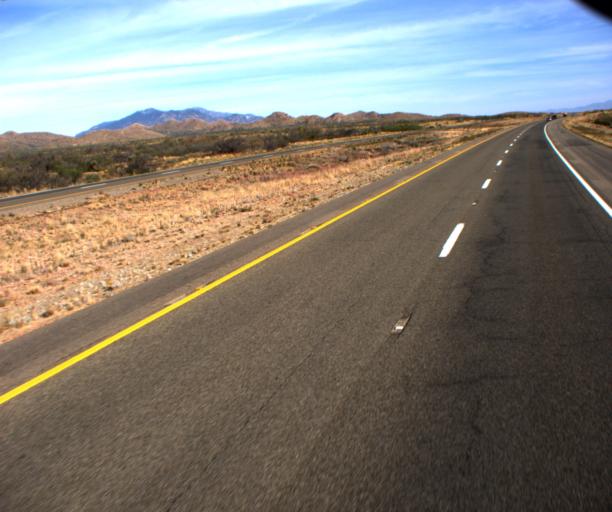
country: US
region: Arizona
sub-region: Graham County
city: Swift Trail Junction
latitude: 32.4740
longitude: -109.6725
